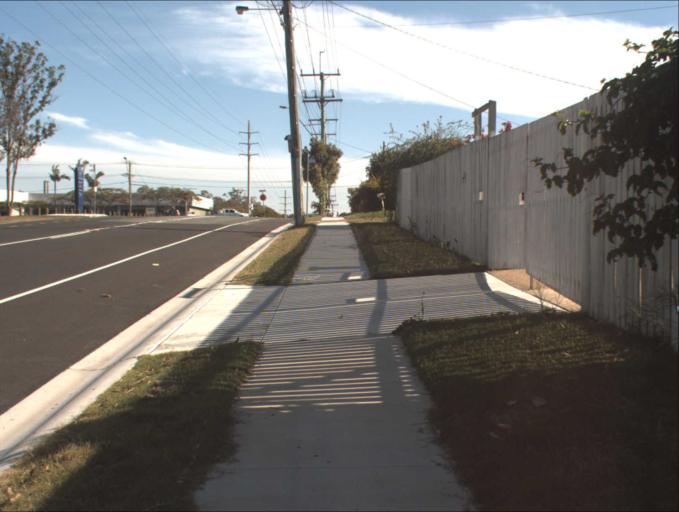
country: AU
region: Queensland
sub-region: Logan
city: Slacks Creek
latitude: -27.6517
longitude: 153.1352
